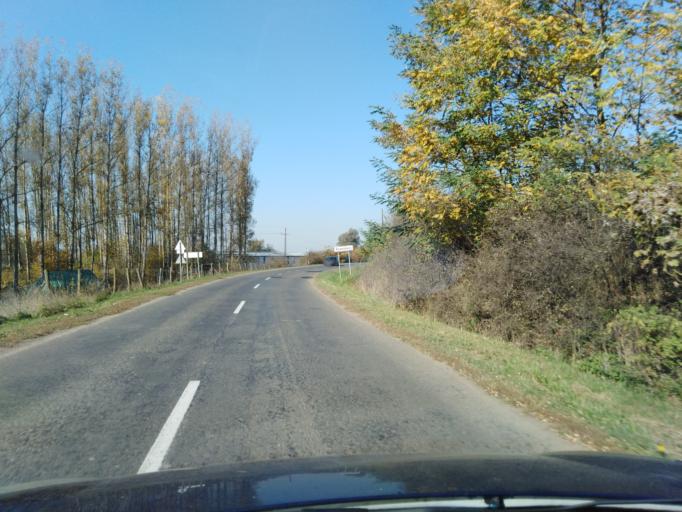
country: HU
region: Nograd
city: Karancskeszi
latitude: 48.1553
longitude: 19.7106
